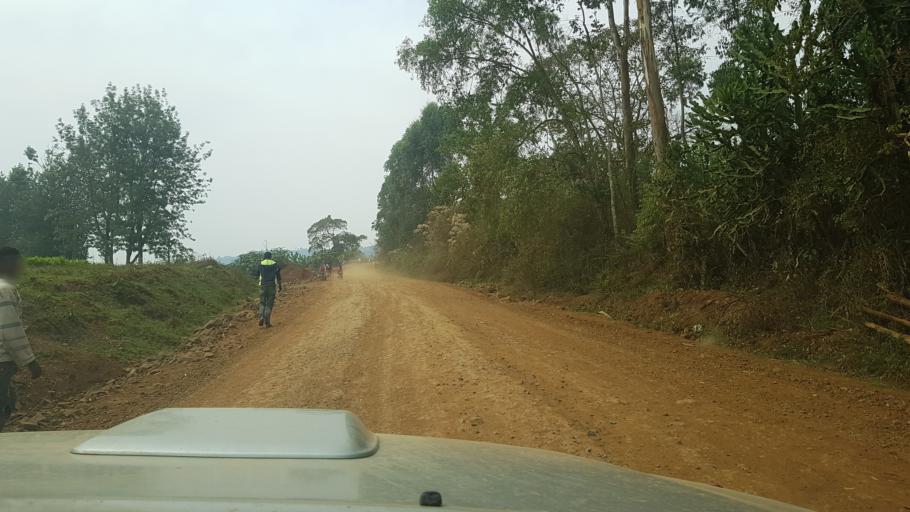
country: ET
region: Oromiya
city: Gore
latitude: 7.8378
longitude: 35.4736
